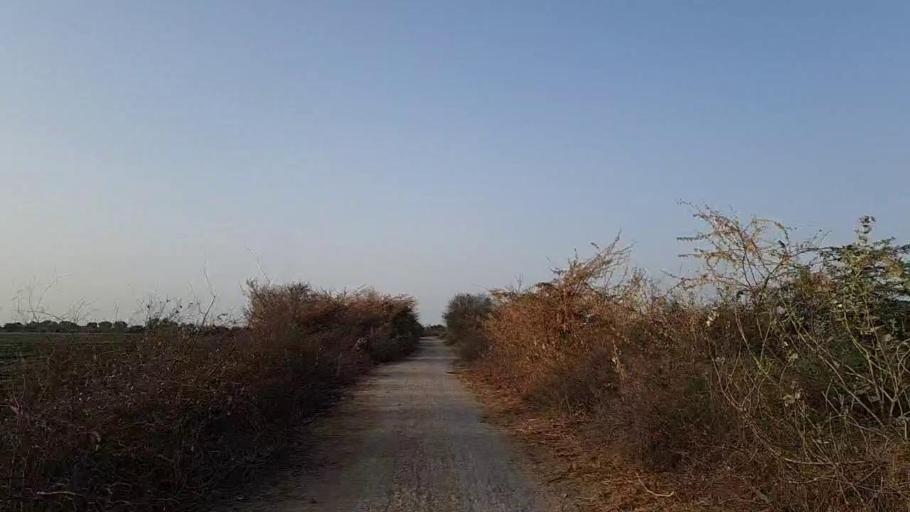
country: PK
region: Sindh
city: Jati
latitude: 24.4074
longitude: 68.1859
